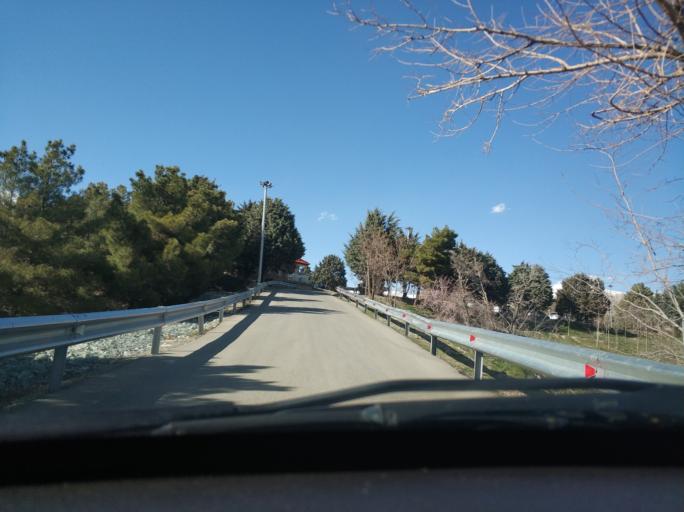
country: IR
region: Tehran
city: Tajrish
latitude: 35.7987
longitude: 51.5663
